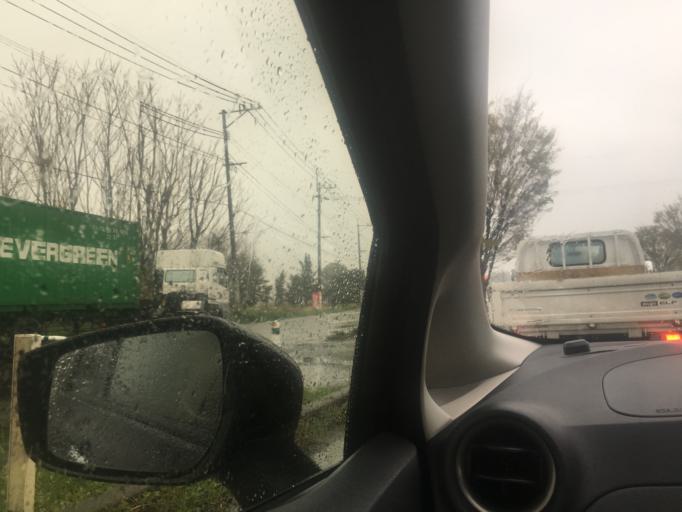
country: JP
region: Kumamoto
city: Ozu
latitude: 32.8005
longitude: 130.7998
